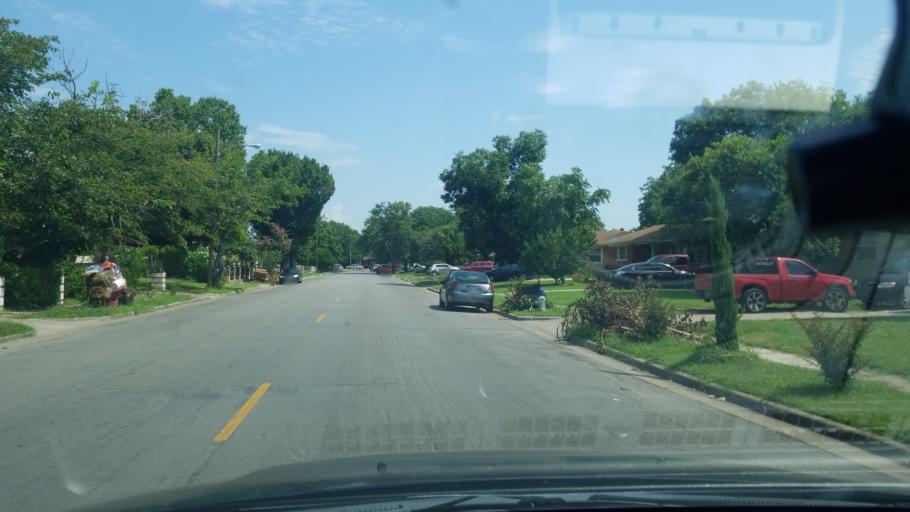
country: US
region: Texas
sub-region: Dallas County
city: Balch Springs
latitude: 32.7467
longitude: -96.6920
